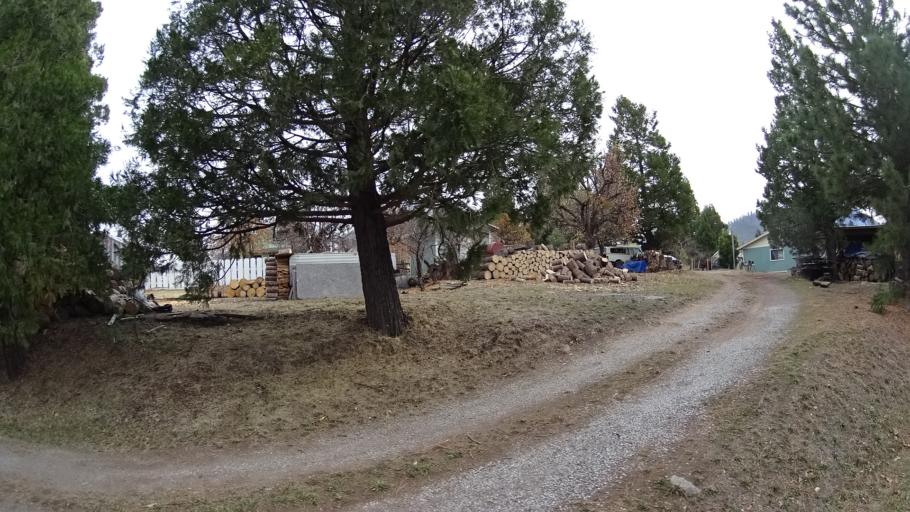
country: US
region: California
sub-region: Siskiyou County
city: Weed
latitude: 41.4275
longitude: -122.3890
